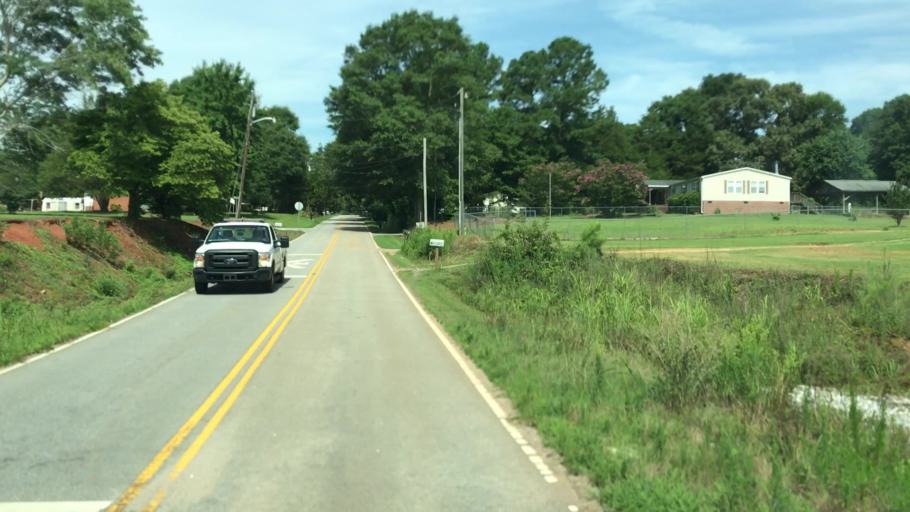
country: US
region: South Carolina
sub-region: Anderson County
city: Williamston
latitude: 34.6310
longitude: -82.4611
